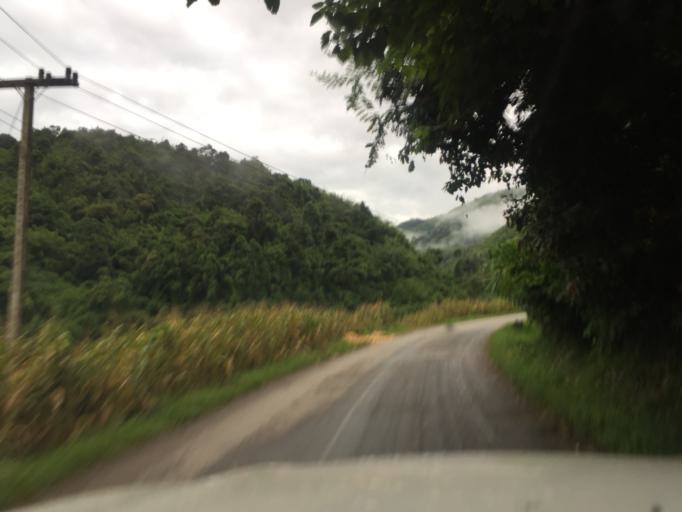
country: LA
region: Oudomxai
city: Muang La
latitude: 20.9503
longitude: 102.2141
